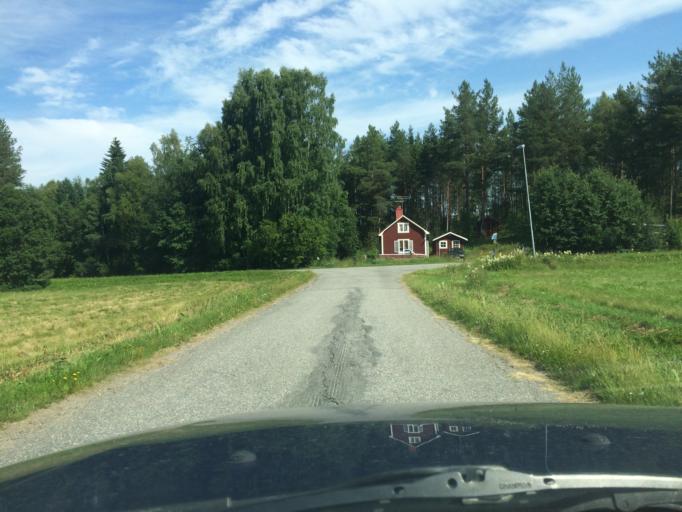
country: SE
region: Norrbotten
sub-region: Pitea Kommun
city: Norrfjarden
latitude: 65.3576
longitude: 21.4197
